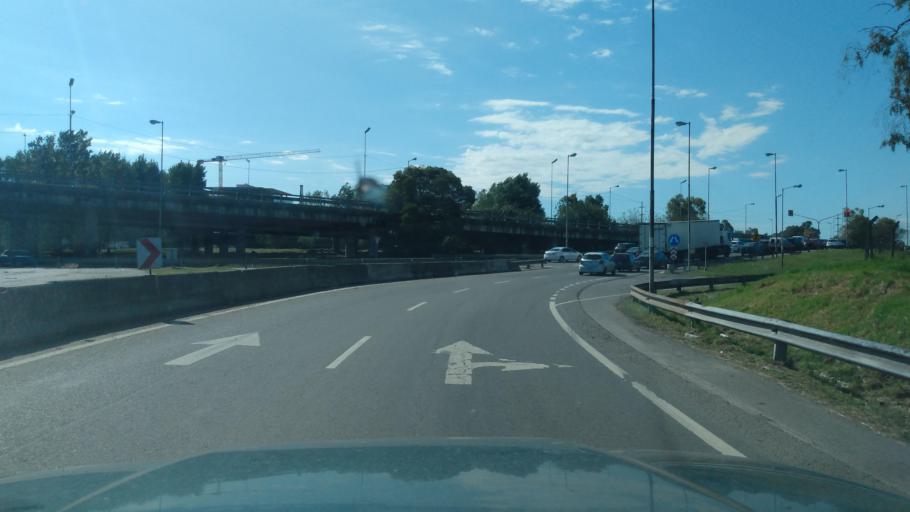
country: AR
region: Buenos Aires
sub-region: Partido de Tigre
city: Tigre
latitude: -34.4883
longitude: -58.5959
